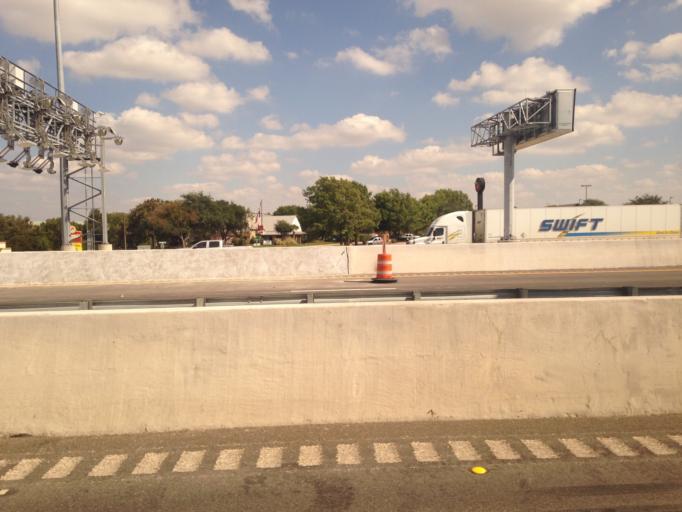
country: US
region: Texas
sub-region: Tarrant County
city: Blue Mound
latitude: 32.8582
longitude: -97.3141
